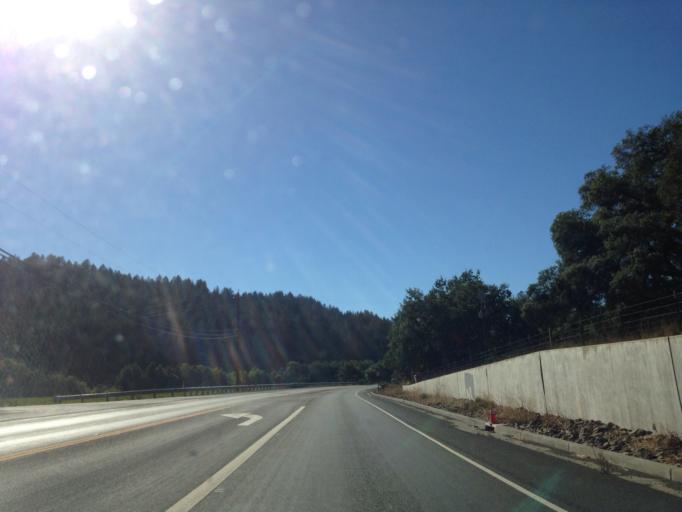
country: US
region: California
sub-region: Sonoma County
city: Forestville
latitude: 38.5030
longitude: -122.9350
